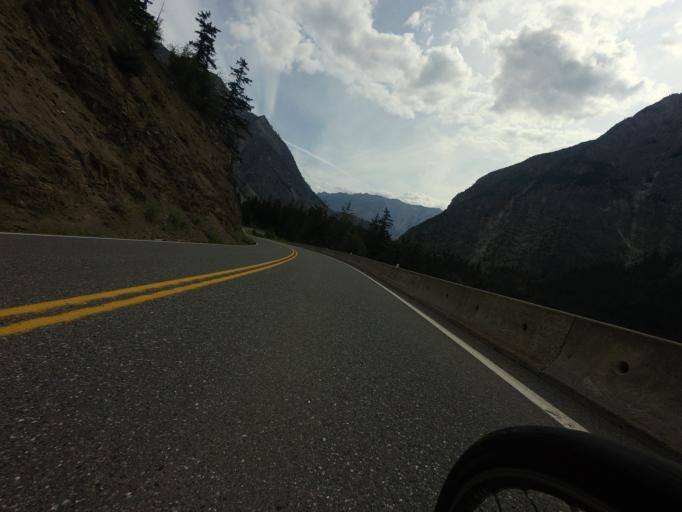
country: CA
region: British Columbia
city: Lillooet
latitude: 50.6589
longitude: -121.9930
